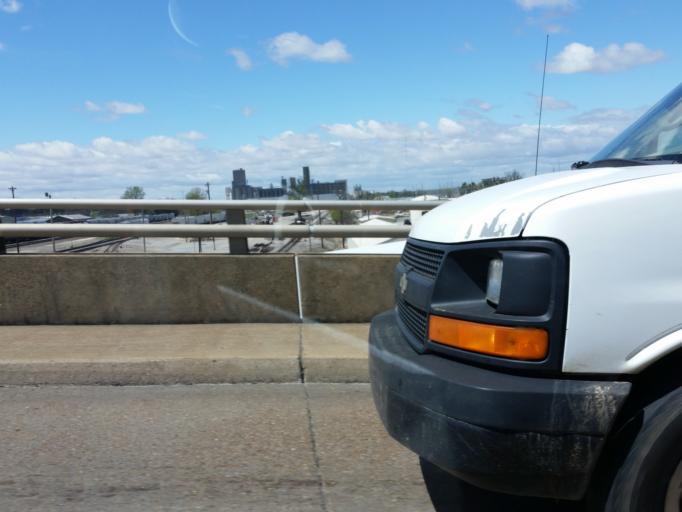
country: US
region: Arkansas
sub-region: Craighead County
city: Jonesboro
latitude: 35.8438
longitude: -90.7049
